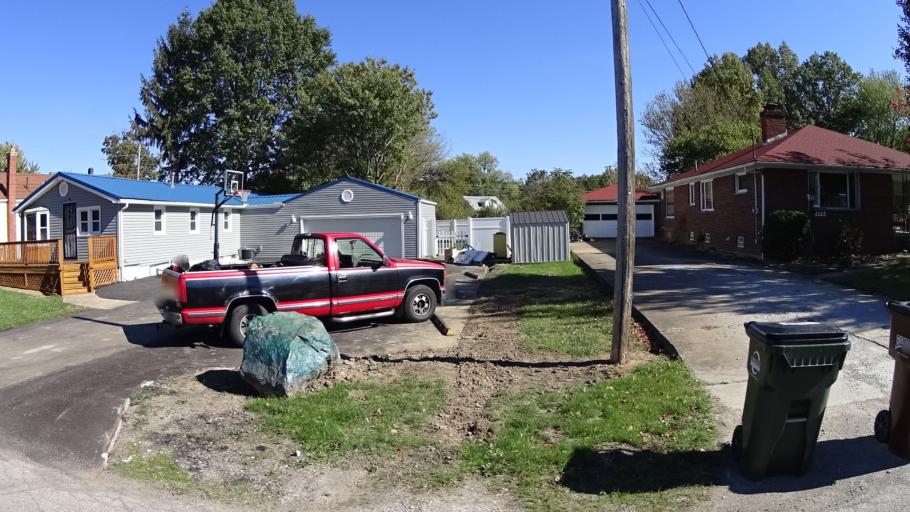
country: US
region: Ohio
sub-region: Lorain County
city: Lorain
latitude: 41.4306
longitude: -82.1574
